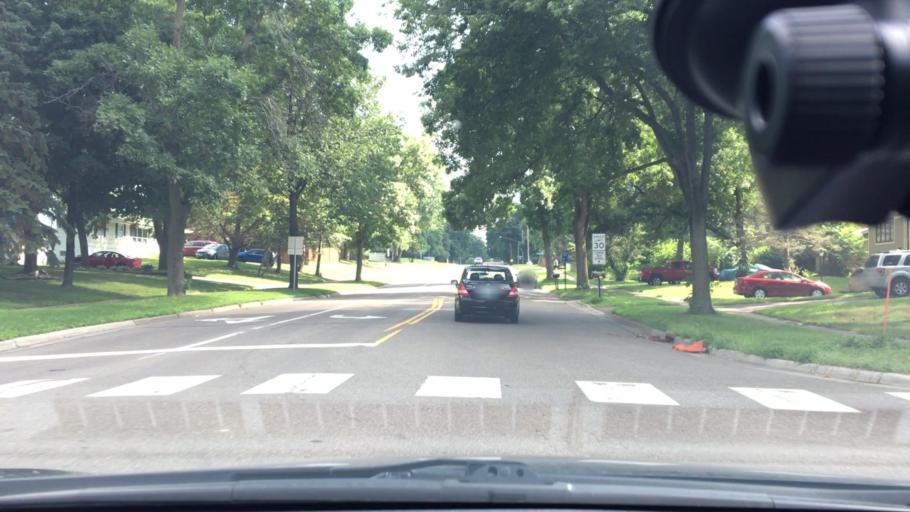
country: US
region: Minnesota
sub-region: Hennepin County
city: New Hope
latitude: 45.0438
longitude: -93.3906
